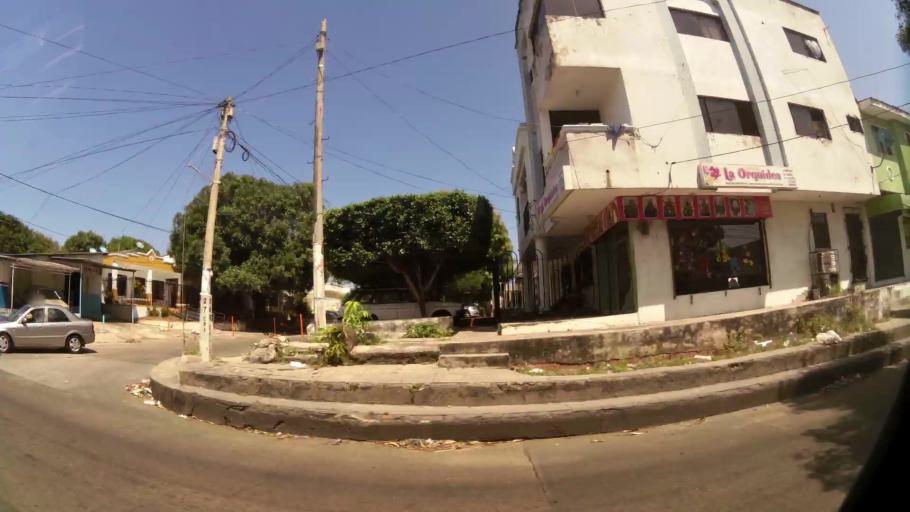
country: CO
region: Atlantico
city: Barranquilla
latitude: 10.9767
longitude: -74.8073
